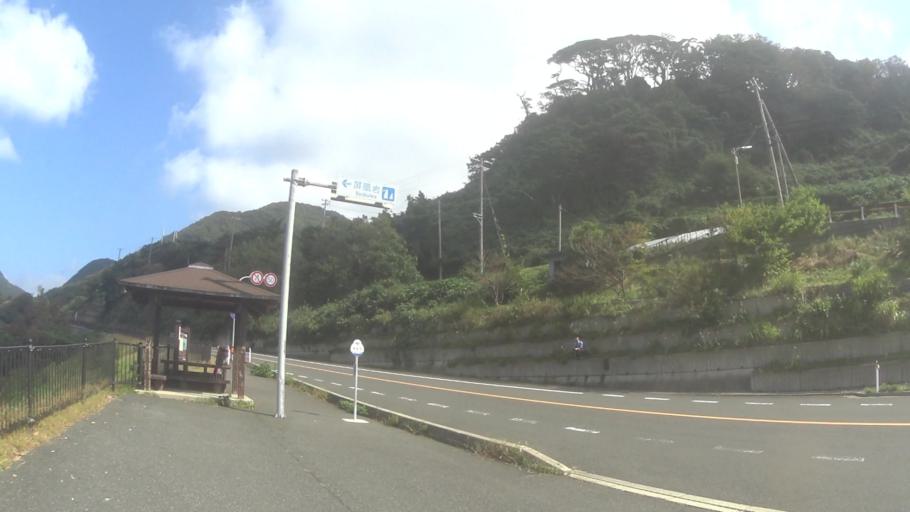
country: JP
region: Kyoto
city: Miyazu
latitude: 35.7453
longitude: 135.1263
